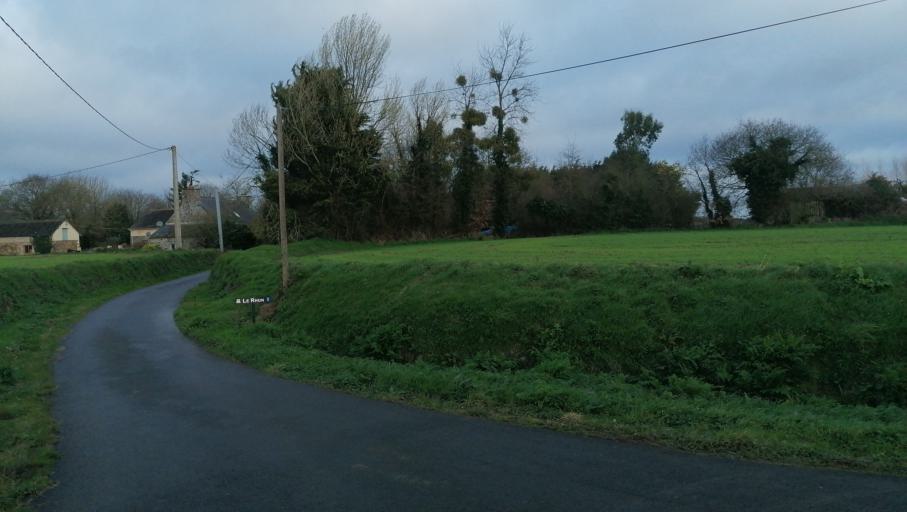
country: FR
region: Brittany
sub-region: Departement des Cotes-d'Armor
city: Pommerit-le-Vicomte
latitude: 48.6449
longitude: -3.0686
